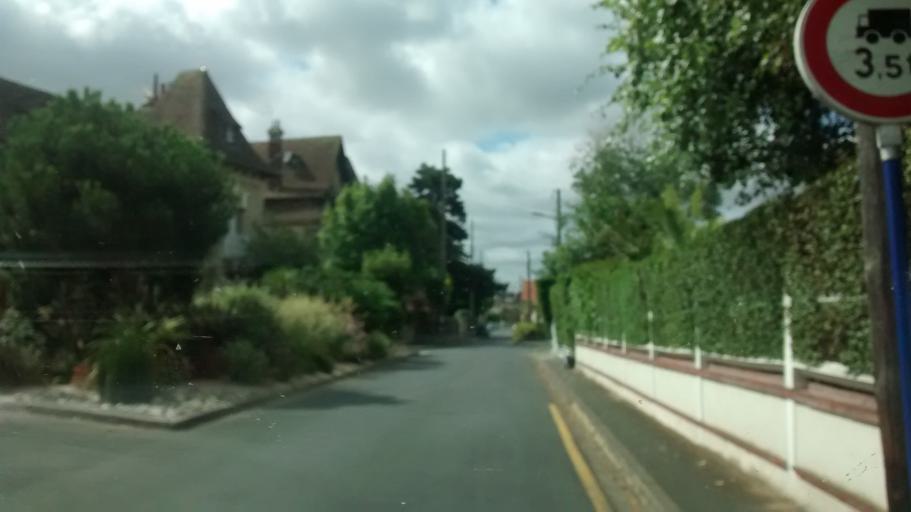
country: FR
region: Lower Normandy
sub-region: Departement du Calvados
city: Ouistreham
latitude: 49.2847
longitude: -0.2578
